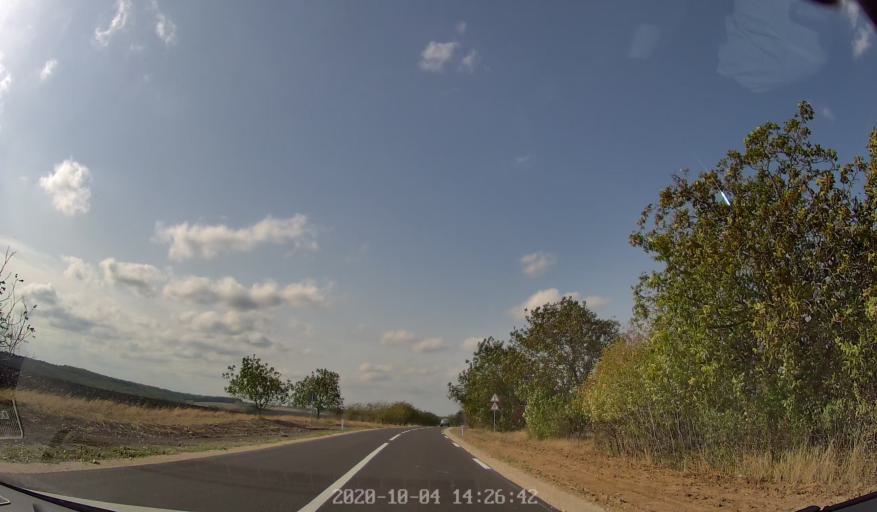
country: MD
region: Rezina
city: Saharna
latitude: 47.6292
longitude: 28.8801
